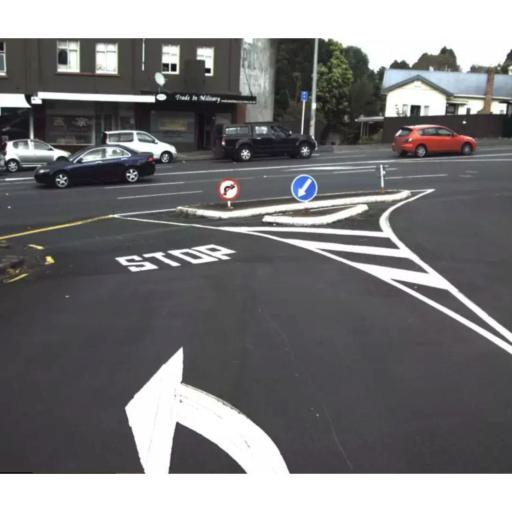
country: NZ
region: Auckland
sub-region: Auckland
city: Auckland
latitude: -36.9089
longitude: 174.7620
